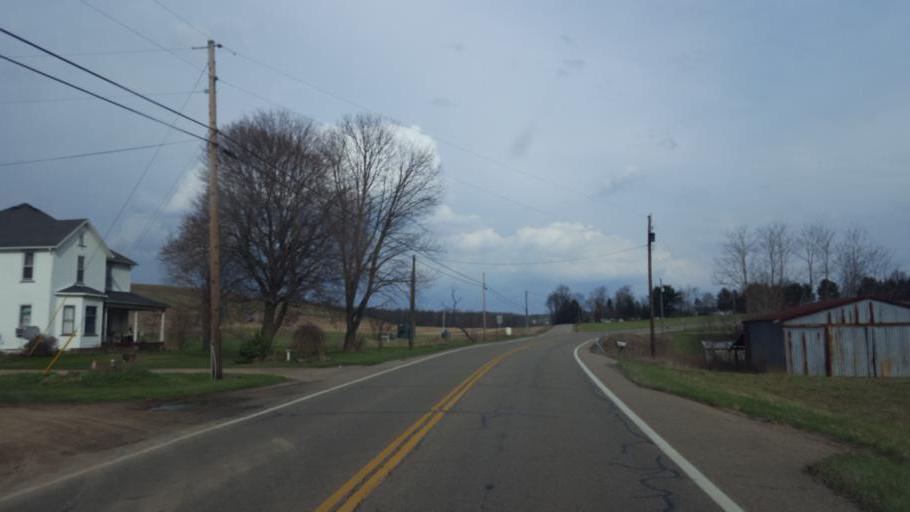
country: US
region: Ohio
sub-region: Coshocton County
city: Coshocton
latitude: 40.2306
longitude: -81.8385
